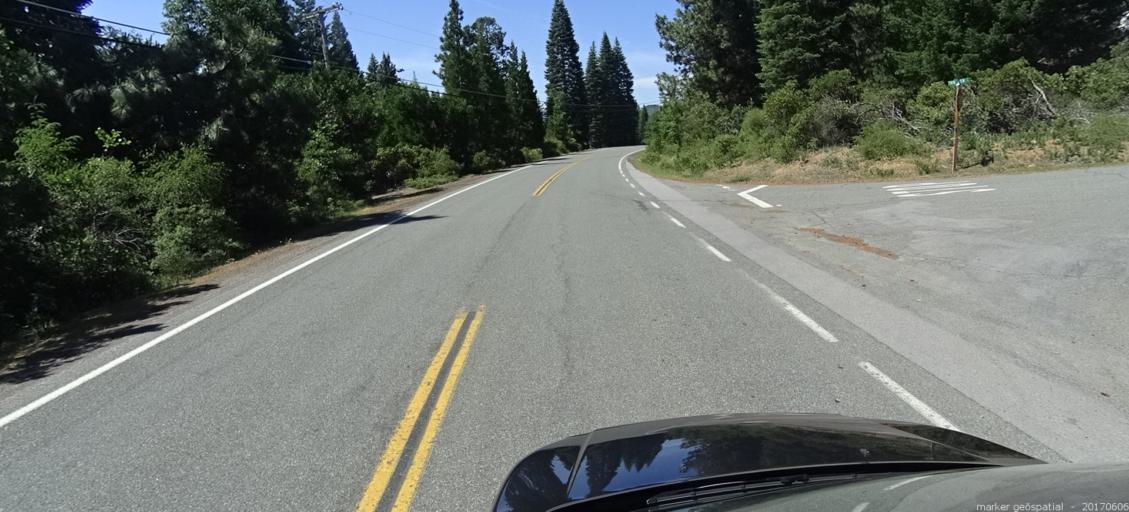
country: US
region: California
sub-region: Siskiyou County
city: Mount Shasta
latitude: 41.2863
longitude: -122.3110
